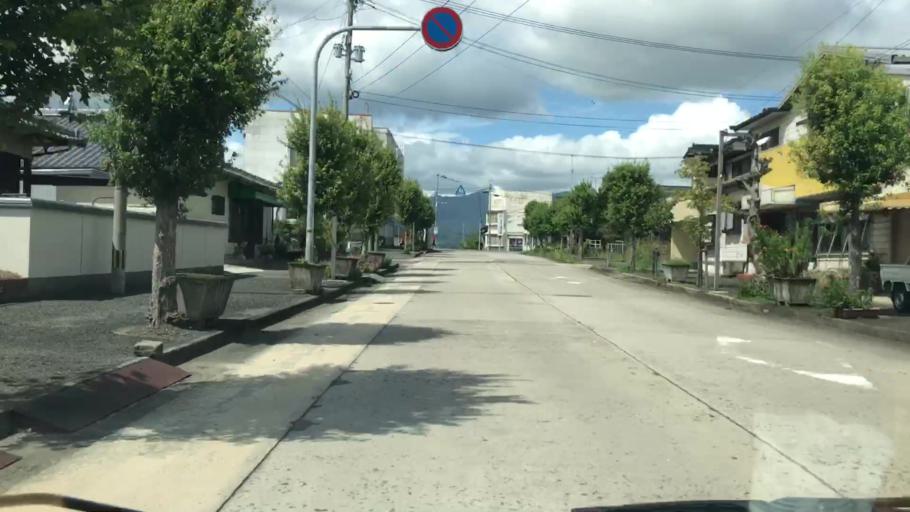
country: JP
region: Saga Prefecture
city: Saga-shi
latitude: 33.2486
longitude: 130.2010
